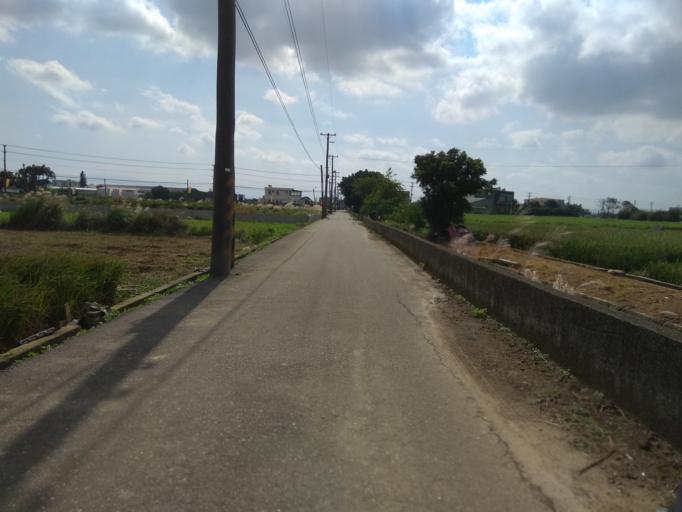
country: TW
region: Taiwan
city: Taoyuan City
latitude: 25.0741
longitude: 121.2489
